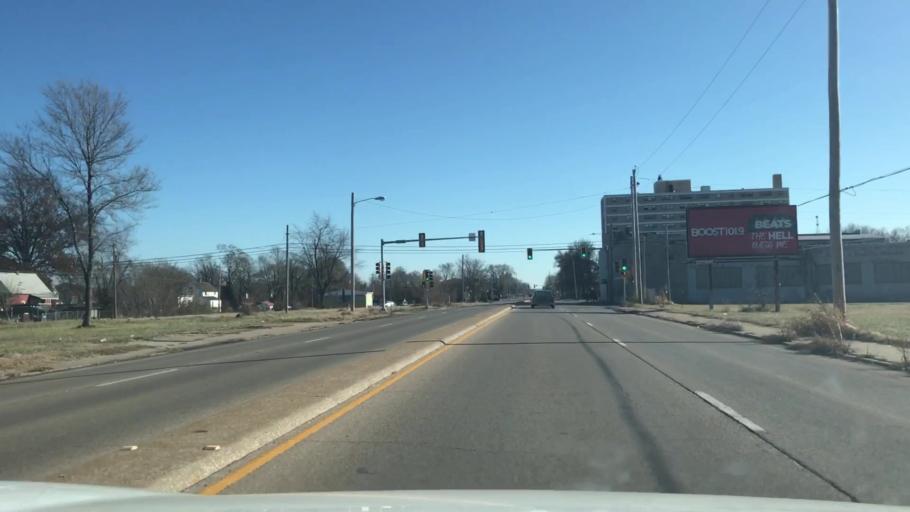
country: US
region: Illinois
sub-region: Saint Clair County
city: East Saint Louis
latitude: 38.6195
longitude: -90.1511
